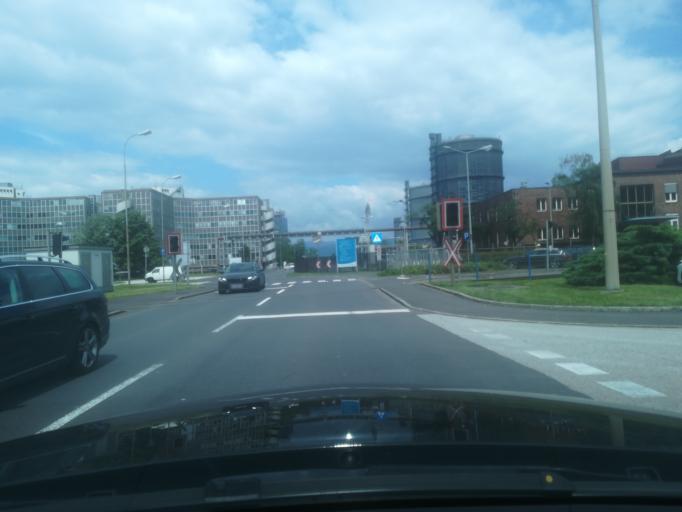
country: AT
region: Upper Austria
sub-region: Politischer Bezirk Urfahr-Umgebung
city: Steyregg
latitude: 48.2733
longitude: 14.3235
